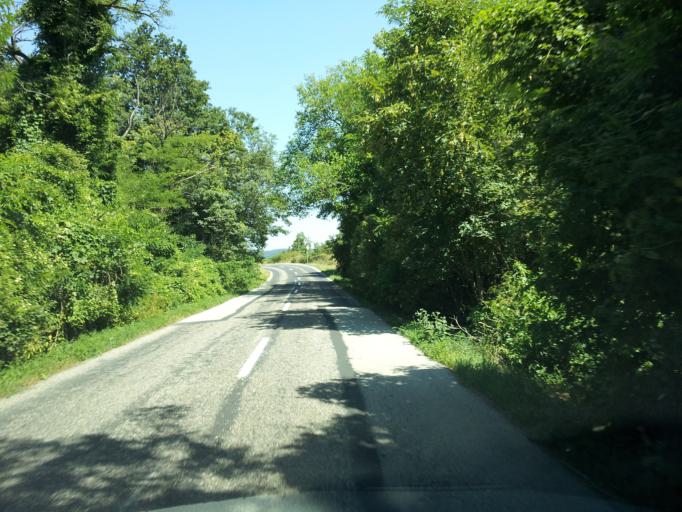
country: HU
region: Fejer
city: Szarliget
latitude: 47.5074
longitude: 18.5498
